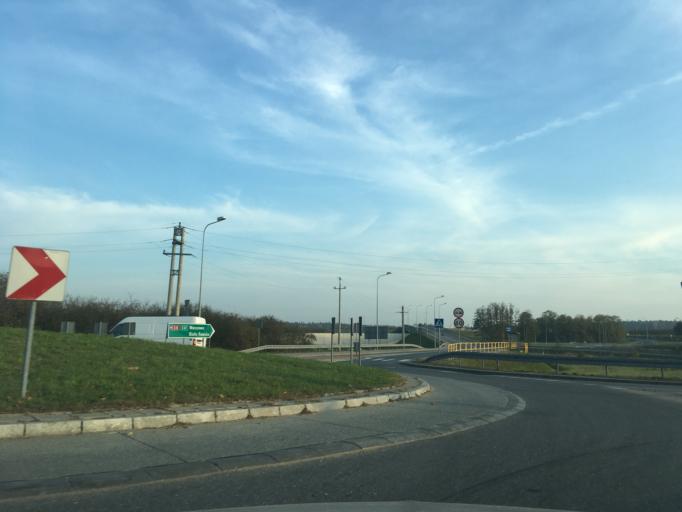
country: PL
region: Lodz Voivodeship
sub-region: Powiat skierniewicki
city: Kowiesy
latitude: 51.9210
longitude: 20.4532
